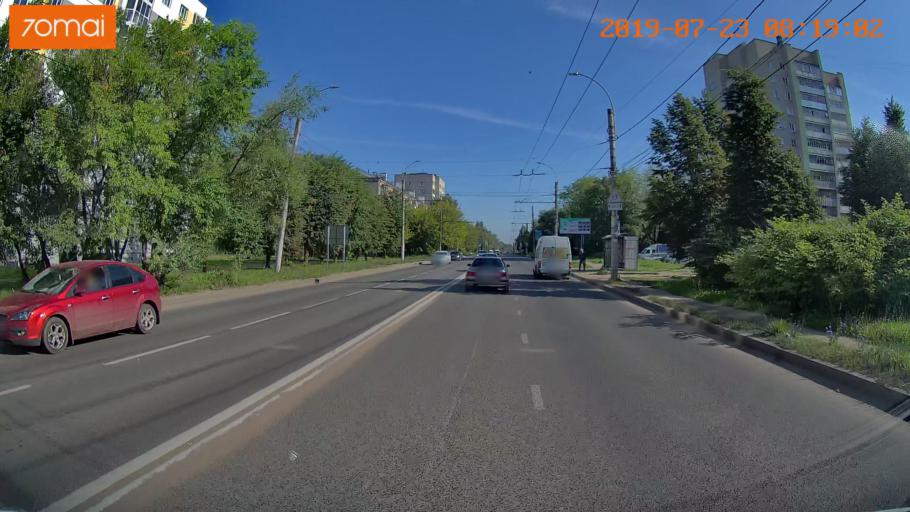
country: RU
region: Ivanovo
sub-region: Gorod Ivanovo
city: Ivanovo
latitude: 56.9656
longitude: 40.9624
